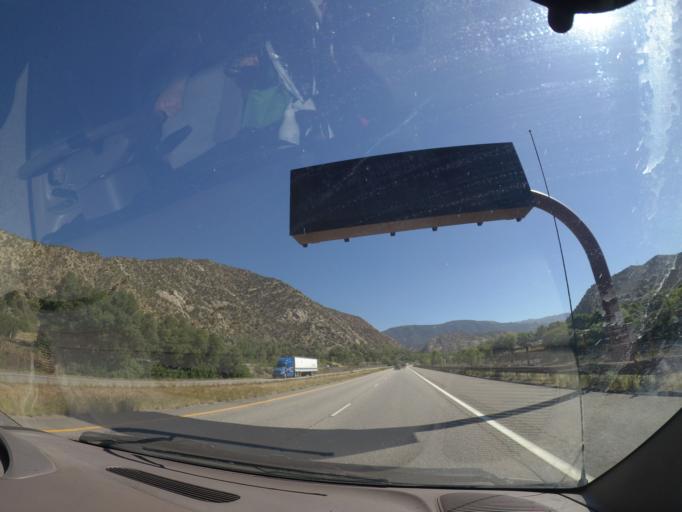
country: US
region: Colorado
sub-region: Garfield County
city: New Castle
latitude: 39.5634
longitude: -107.5524
